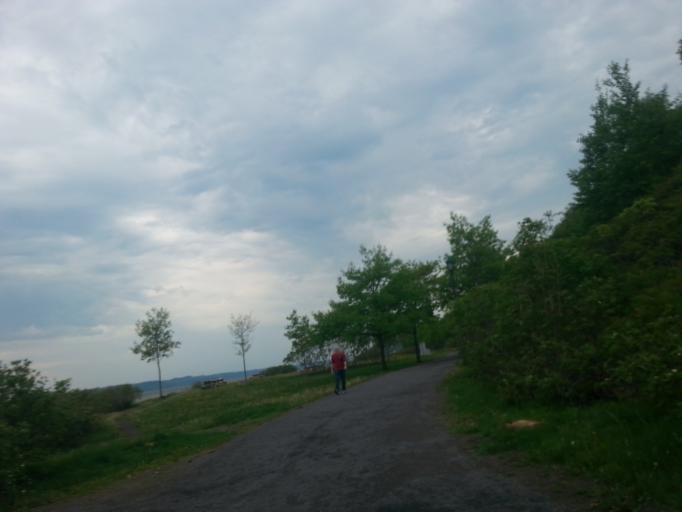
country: CA
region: Quebec
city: L'Ancienne-Lorette
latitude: 46.7491
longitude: -71.3261
